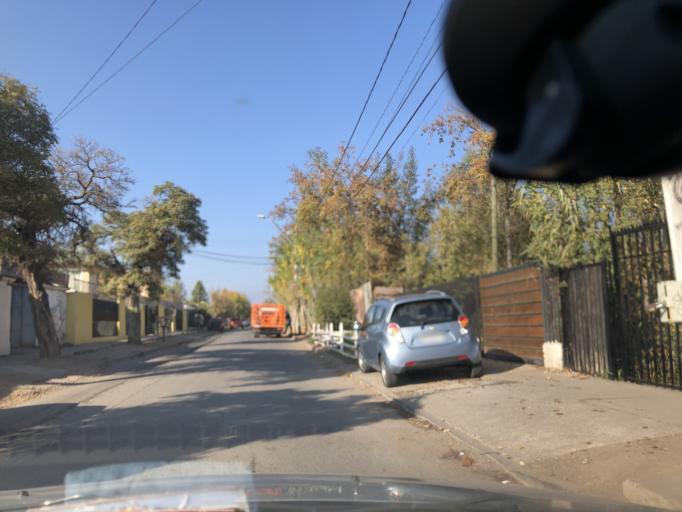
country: CL
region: Santiago Metropolitan
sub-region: Provincia de Cordillera
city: Puente Alto
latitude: -33.6236
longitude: -70.5858
